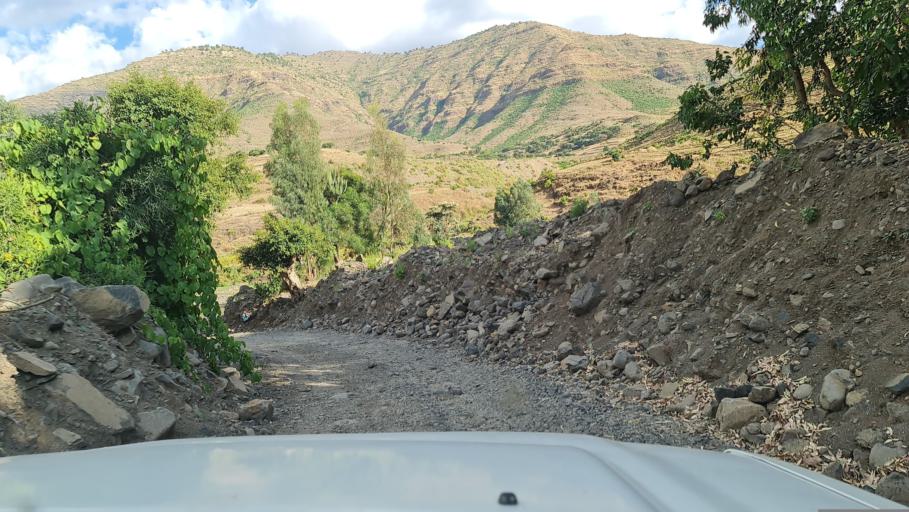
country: ET
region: Amhara
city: Debark'
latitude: 13.0820
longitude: 38.0112
